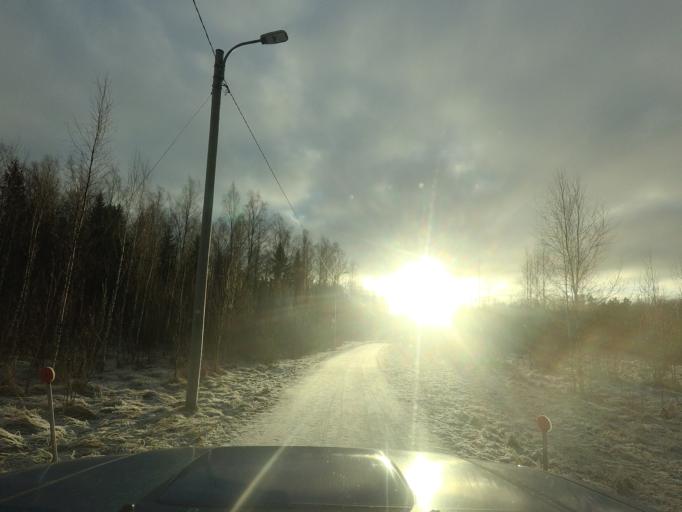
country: FI
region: Uusimaa
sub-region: Helsinki
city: Espoo
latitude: 60.1898
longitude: 24.6557
